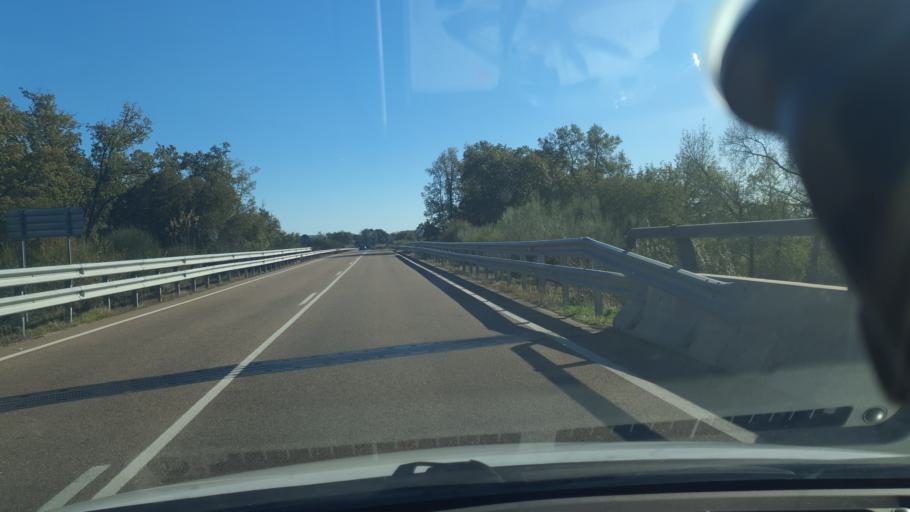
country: ES
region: Castille and Leon
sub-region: Provincia de Avila
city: Candeleda
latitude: 40.1388
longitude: -5.2508
